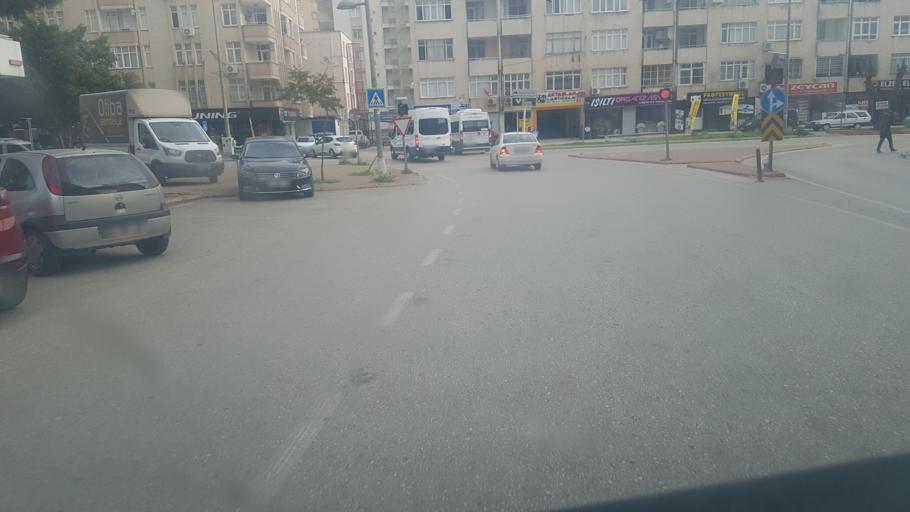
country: TR
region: Adana
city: Adana
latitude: 37.0270
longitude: 35.3106
